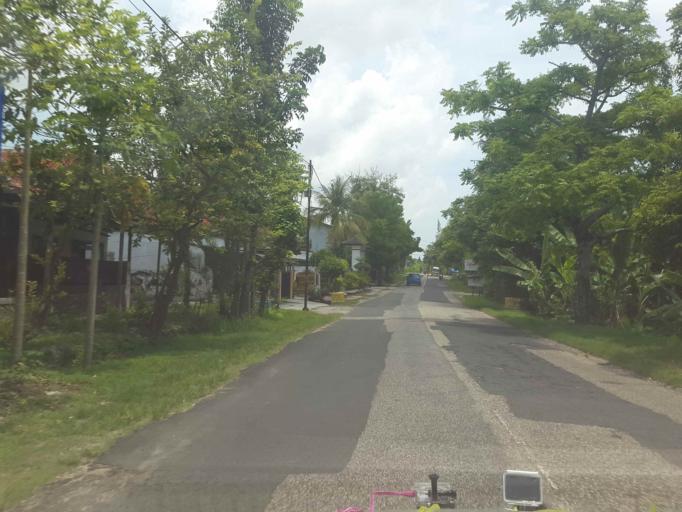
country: ID
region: East Java
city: Pesisir
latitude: -7.1152
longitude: 113.7516
